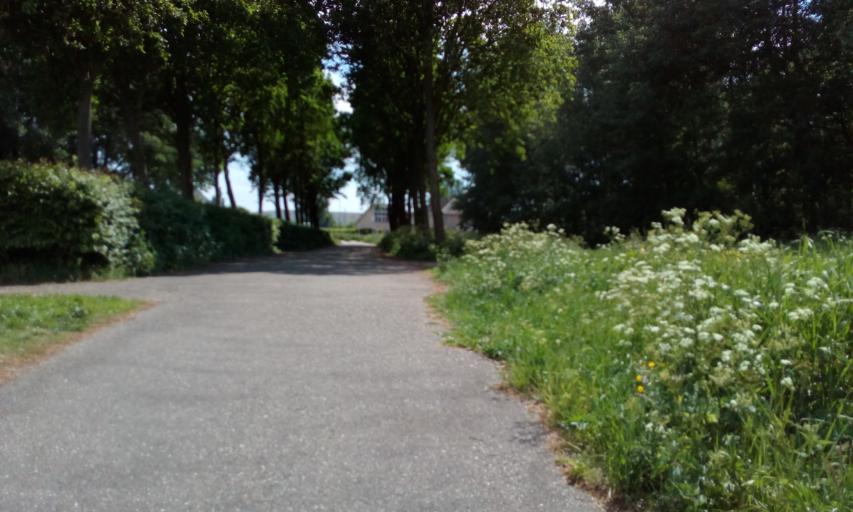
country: NL
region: South Holland
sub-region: Gemeente Pijnacker-Nootdorp
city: Pijnacker
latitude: 52.0408
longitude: 4.4585
